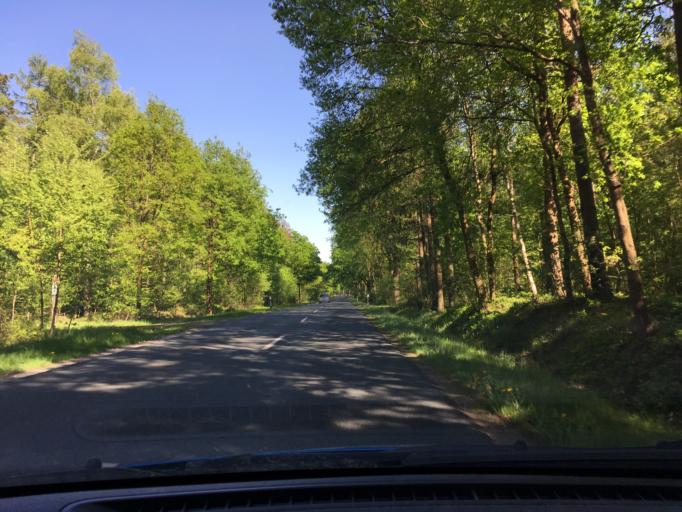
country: DE
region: Lower Saxony
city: Radbruch
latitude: 53.3149
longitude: 10.2620
